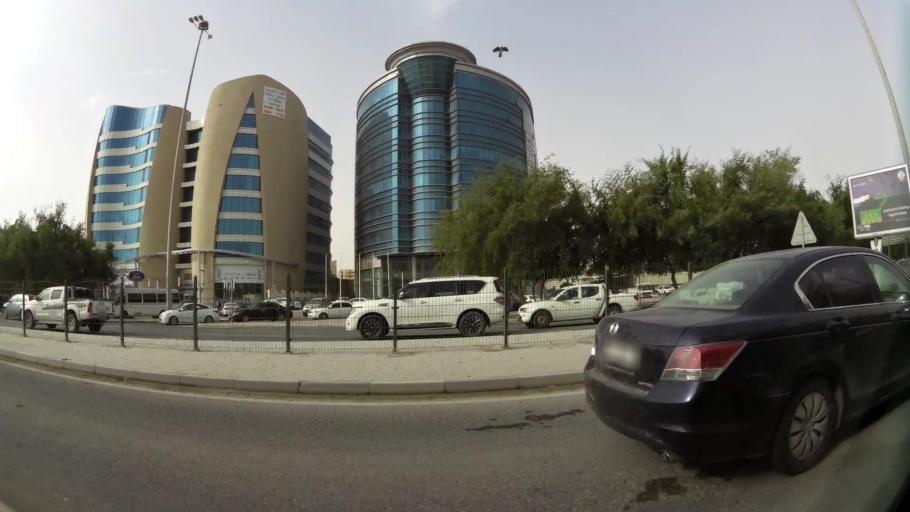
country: QA
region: Baladiyat ad Dawhah
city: Doha
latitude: 25.2704
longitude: 51.5473
